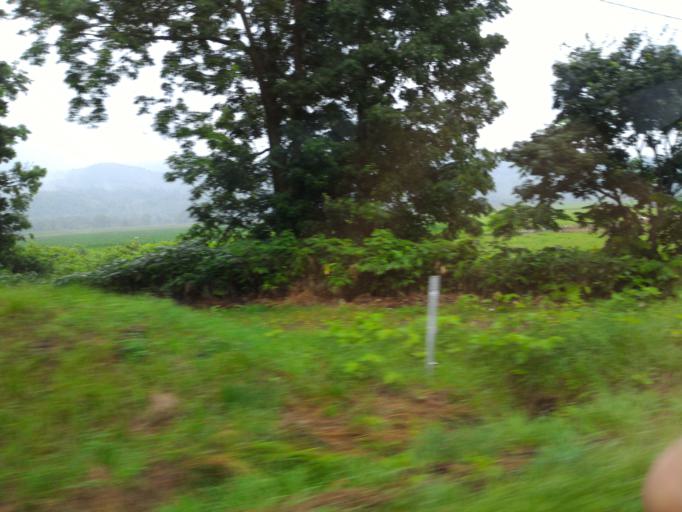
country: JP
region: Hokkaido
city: Nayoro
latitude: 44.5726
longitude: 142.3132
